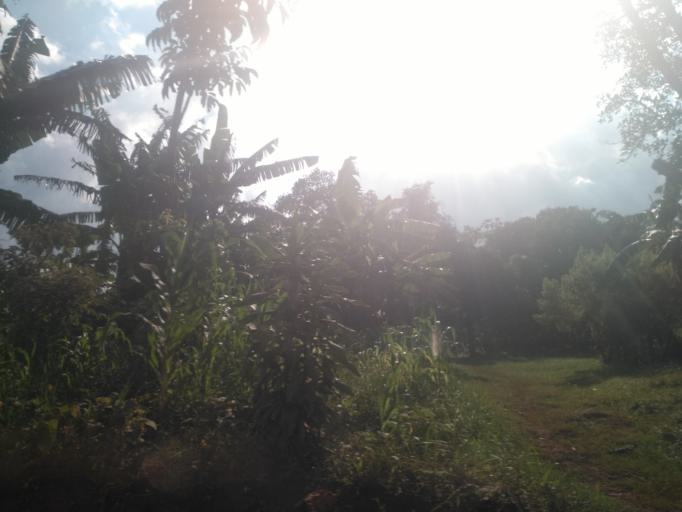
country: UG
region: Central Region
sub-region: Wakiso District
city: Kajansi
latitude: 0.2636
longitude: 32.4387
